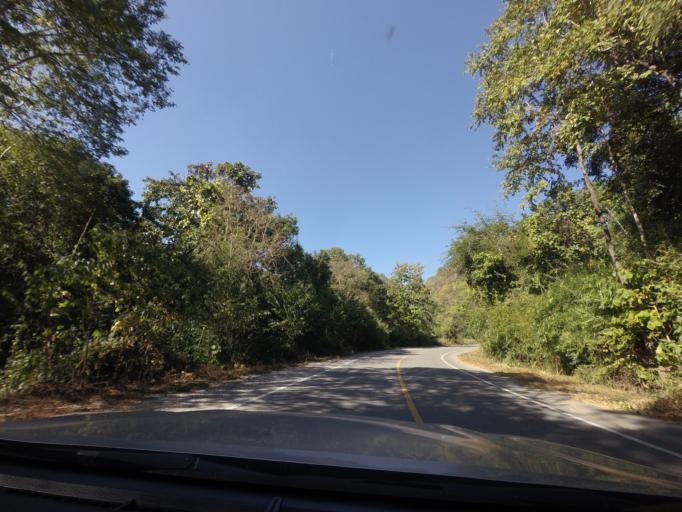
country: TH
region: Lampang
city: Chae Hom
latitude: 18.5528
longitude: 99.6250
